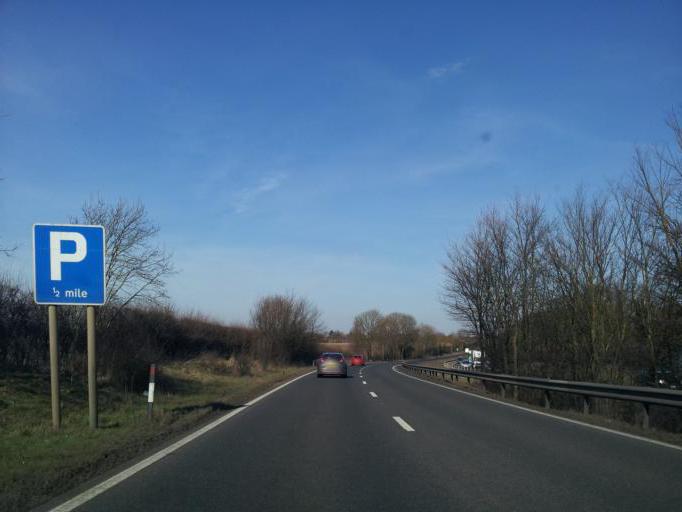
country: GB
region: England
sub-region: Cambridgeshire
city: Buckden
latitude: 52.2801
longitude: -0.2589
